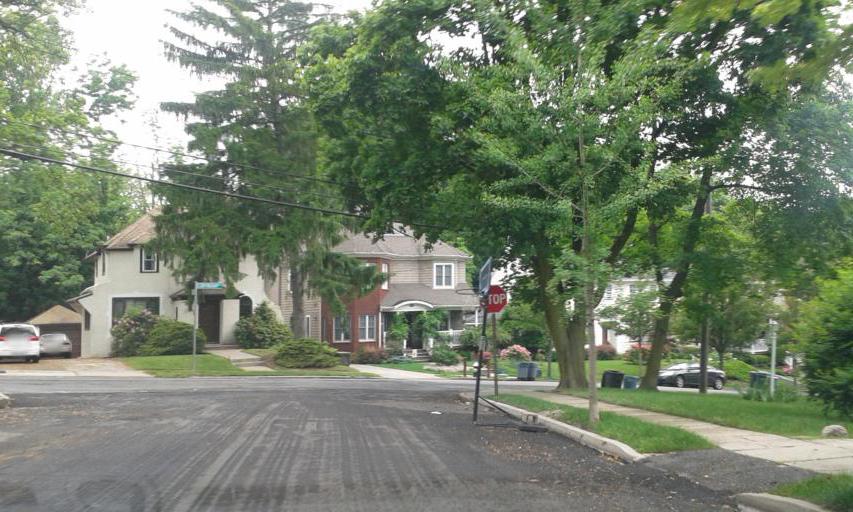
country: US
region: New Jersey
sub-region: Hudson County
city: Bayonne
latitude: 40.6362
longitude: -74.1022
